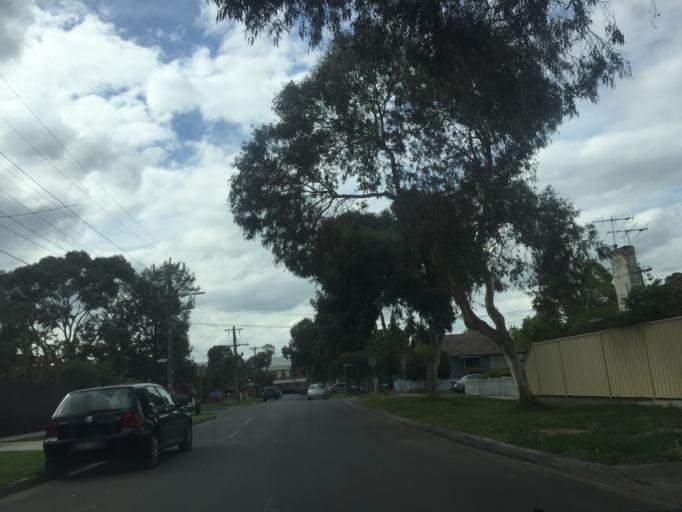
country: AU
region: Victoria
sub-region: Darebin
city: Preston
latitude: -37.7561
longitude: 145.0228
